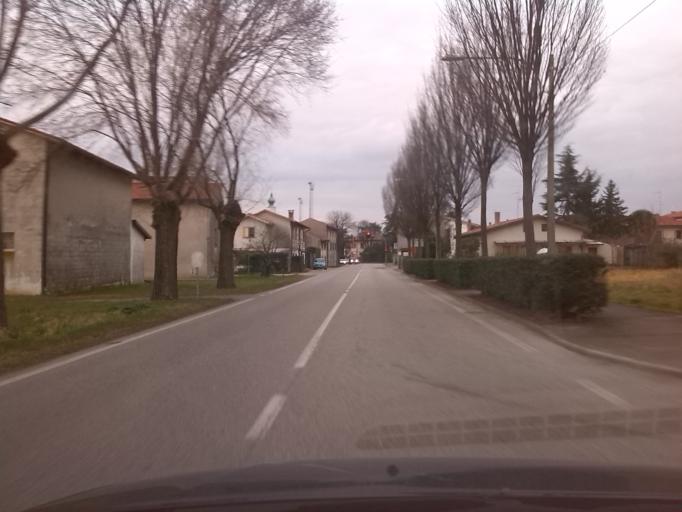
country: IT
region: Friuli Venezia Giulia
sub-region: Provincia di Gorizia
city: Romans d'Isonzo
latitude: 45.8863
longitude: 13.4409
